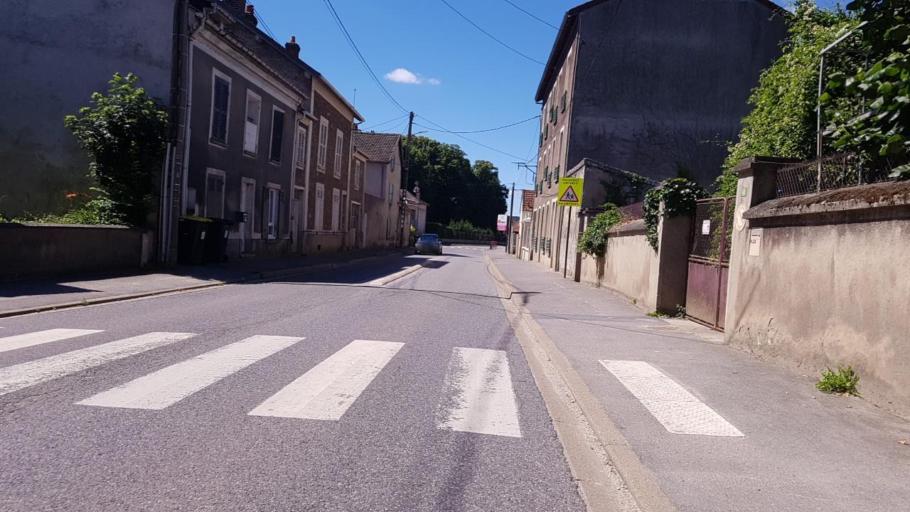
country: FR
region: Ile-de-France
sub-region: Departement de Seine-et-Marne
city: Chamigny
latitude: 48.9599
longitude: 3.1445
